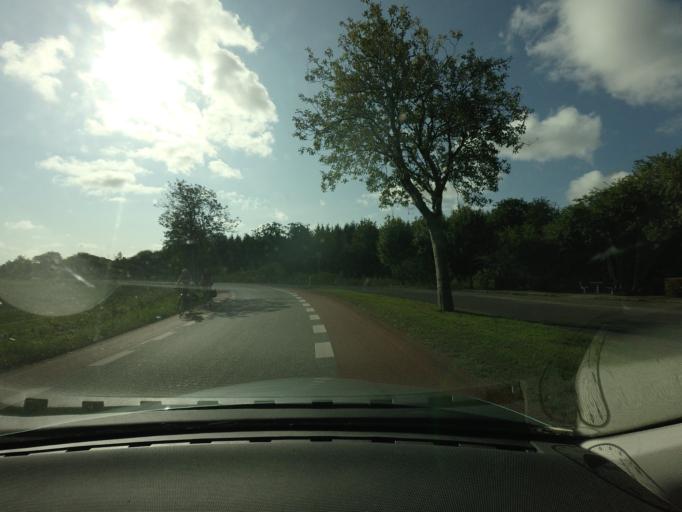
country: DK
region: Zealand
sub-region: Vordingborg Kommune
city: Praesto
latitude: 55.1450
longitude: 12.0078
